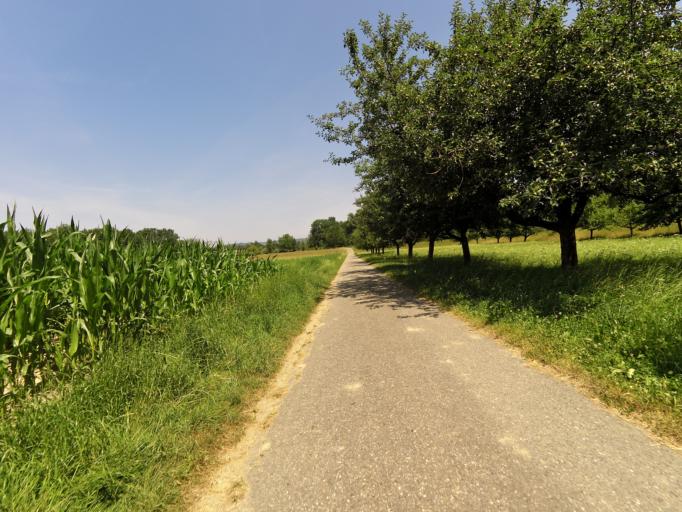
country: CH
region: Thurgau
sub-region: Frauenfeld District
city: Mullheim
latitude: 47.5816
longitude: 9.0070
